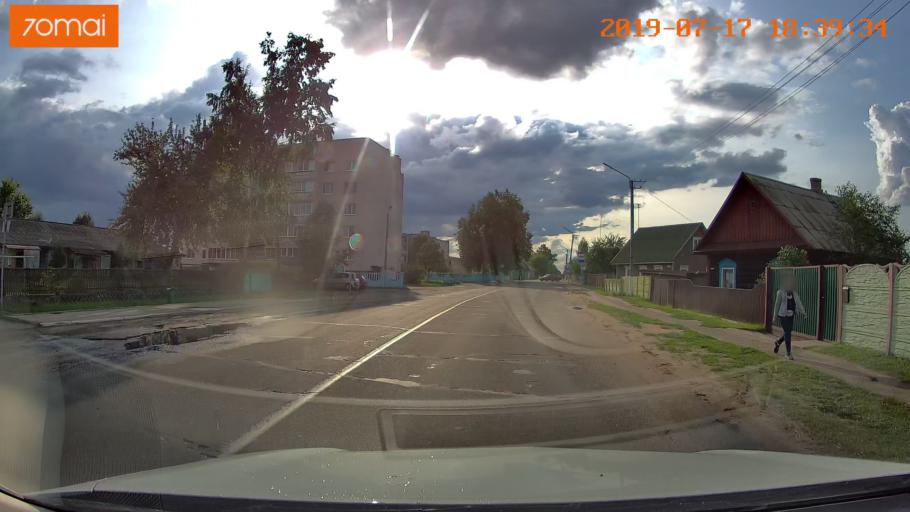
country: BY
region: Mogilev
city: Asipovichy
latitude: 53.2981
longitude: 28.6557
